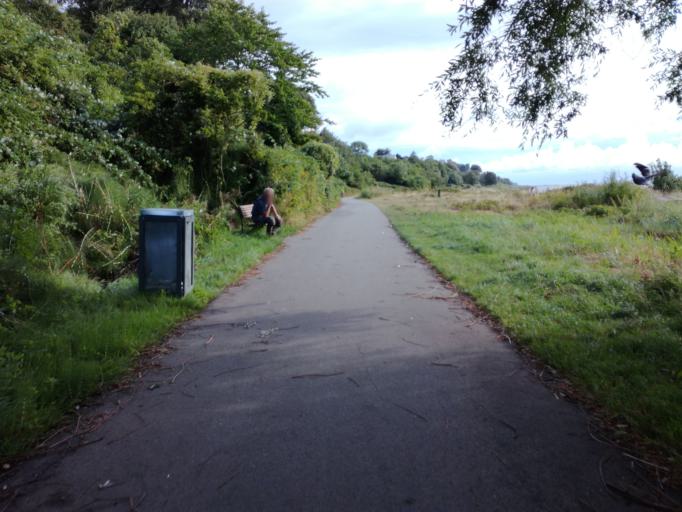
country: DK
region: South Denmark
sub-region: Fredericia Kommune
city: Fredericia
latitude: 55.5732
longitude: 9.7751
